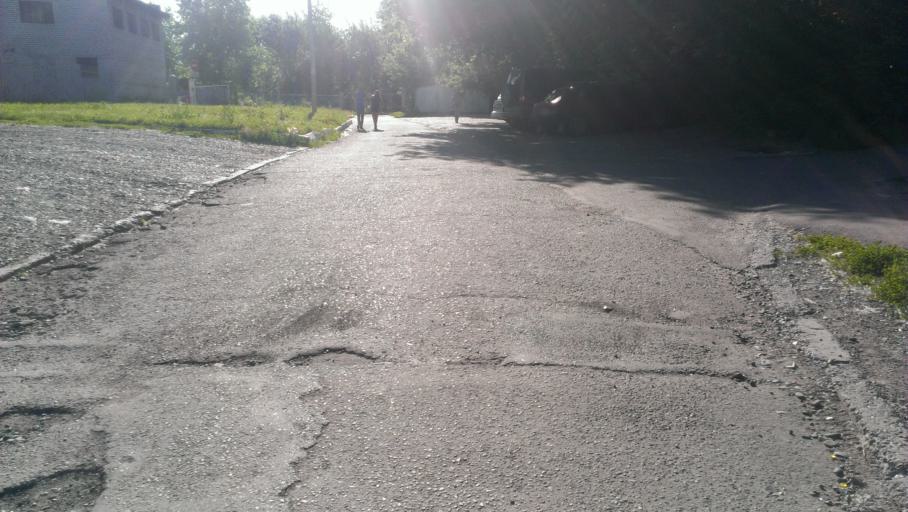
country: RU
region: Altai Krai
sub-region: Gorod Barnaulskiy
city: Barnaul
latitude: 53.3669
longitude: 83.7018
